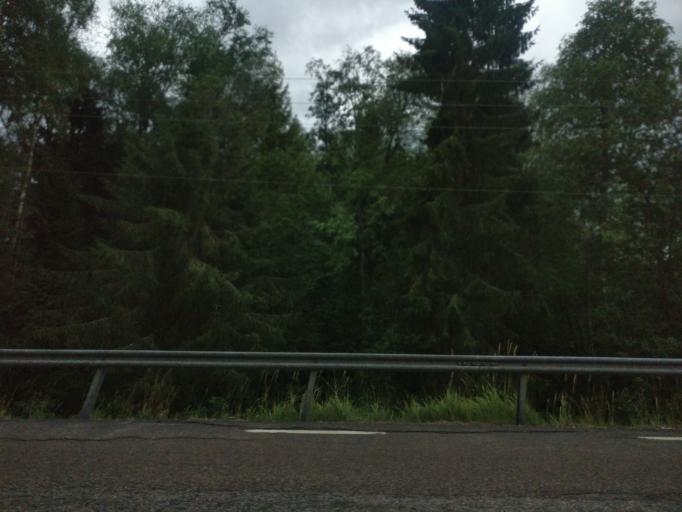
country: SE
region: Vaermland
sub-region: Torsby Kommun
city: Torsby
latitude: 60.6296
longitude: 13.0216
